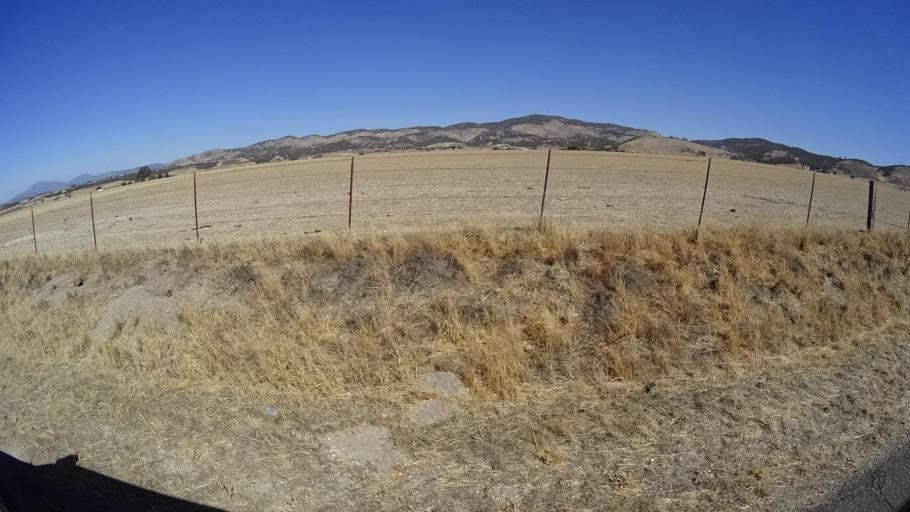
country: US
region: California
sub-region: Monterey County
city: King City
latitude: 35.9658
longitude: -121.0943
